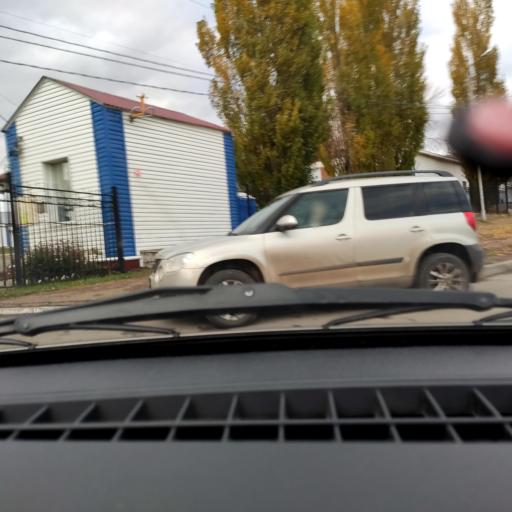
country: RU
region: Bashkortostan
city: Ufa
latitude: 54.7421
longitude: 55.9463
